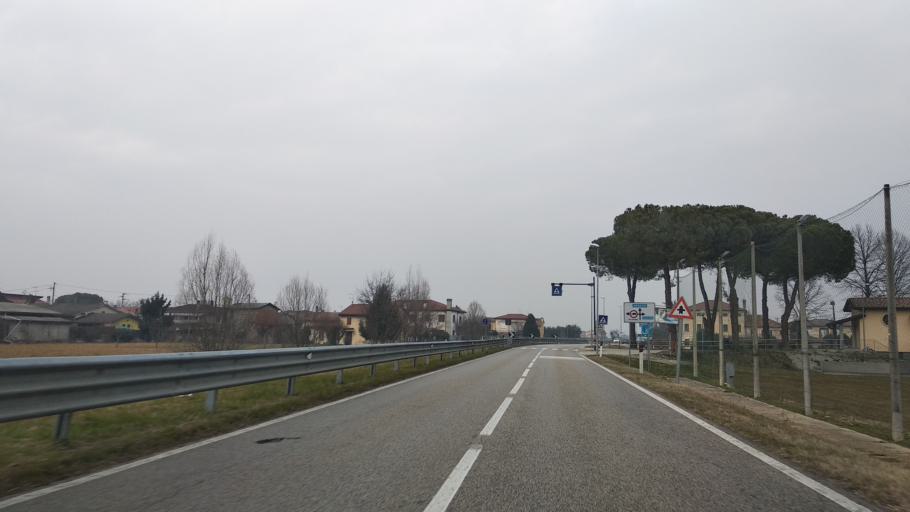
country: IT
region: Veneto
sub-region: Provincia di Padova
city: Santa Maria di Non
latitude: 45.5208
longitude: 11.8671
